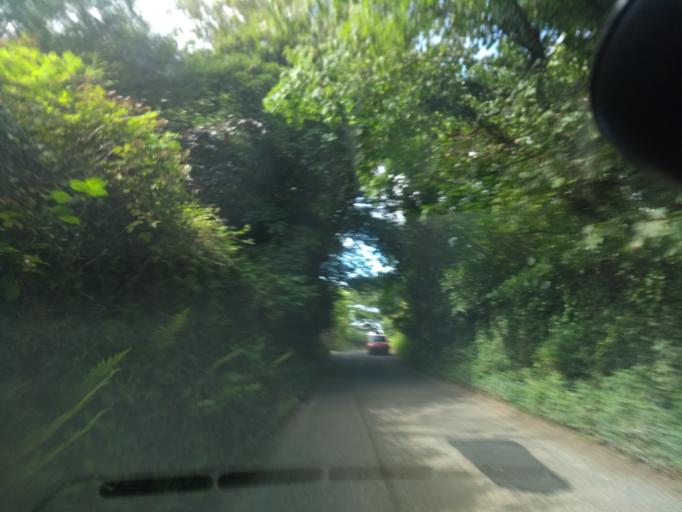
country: GB
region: England
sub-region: Devon
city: Modbury
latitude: 50.3054
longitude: -3.8855
